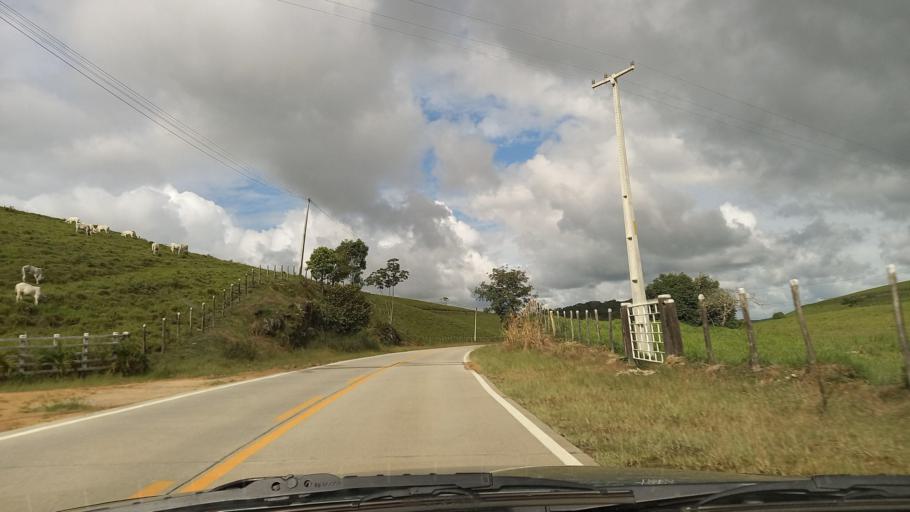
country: BR
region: Pernambuco
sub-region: Quipapa
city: Quipapa
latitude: -8.7773
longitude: -35.9232
